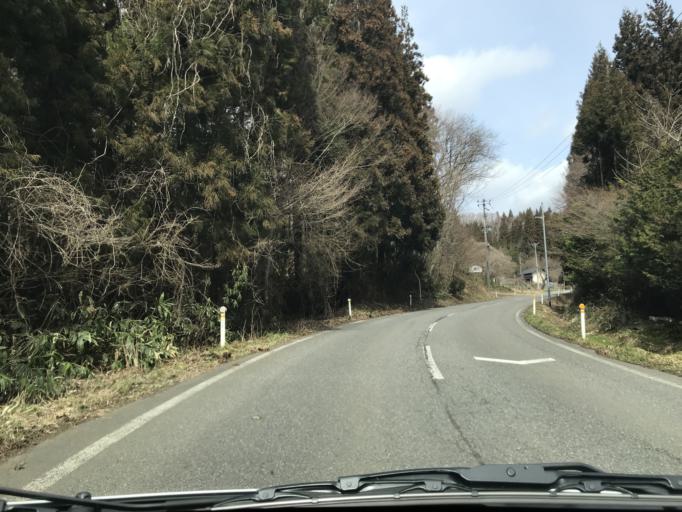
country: JP
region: Iwate
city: Kitakami
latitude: 39.2440
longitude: 141.3182
